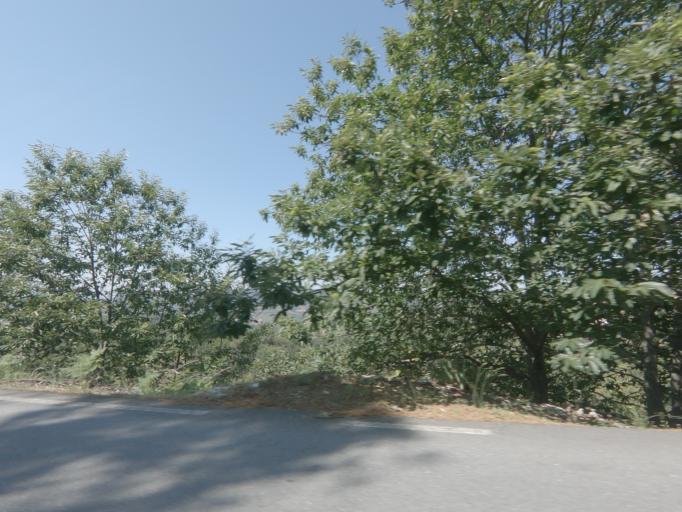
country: PT
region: Viseu
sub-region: Tarouca
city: Tarouca
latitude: 41.0343
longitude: -7.7296
